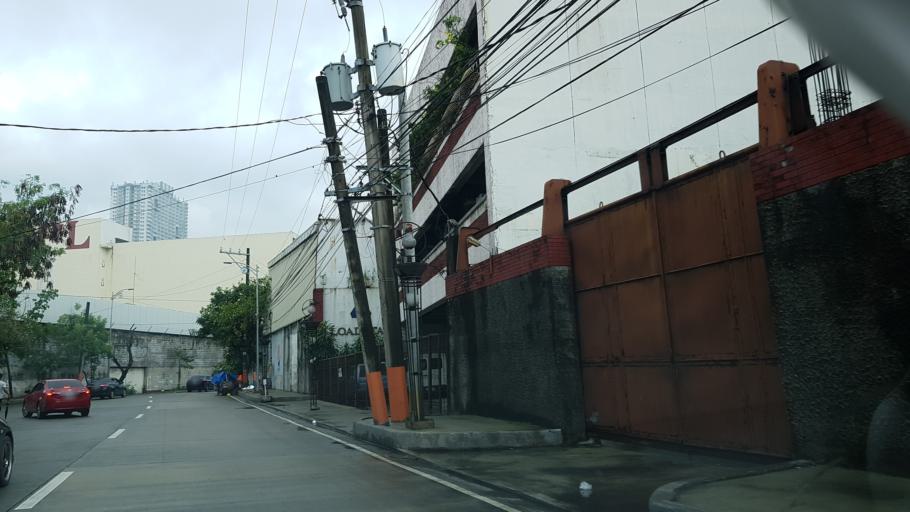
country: PH
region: Metro Manila
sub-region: City of Manila
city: Quiapo
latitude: 14.5819
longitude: 120.9893
